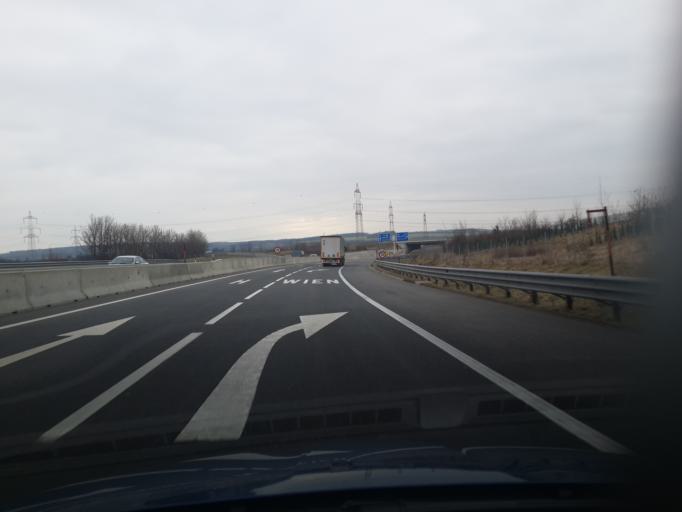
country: AT
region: Burgenland
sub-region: Politischer Bezirk Neusiedl am See
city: Parndorf
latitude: 48.0216
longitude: 16.8415
